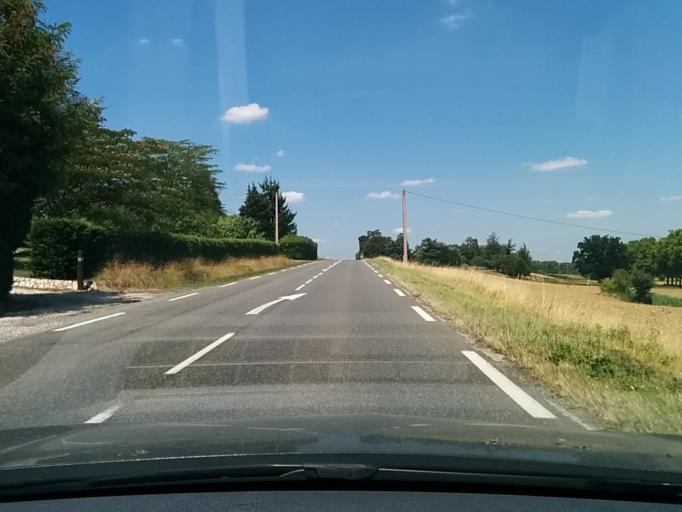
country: FR
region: Midi-Pyrenees
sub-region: Departement du Gers
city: Vic-Fezensac
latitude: 43.7285
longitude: 0.3755
